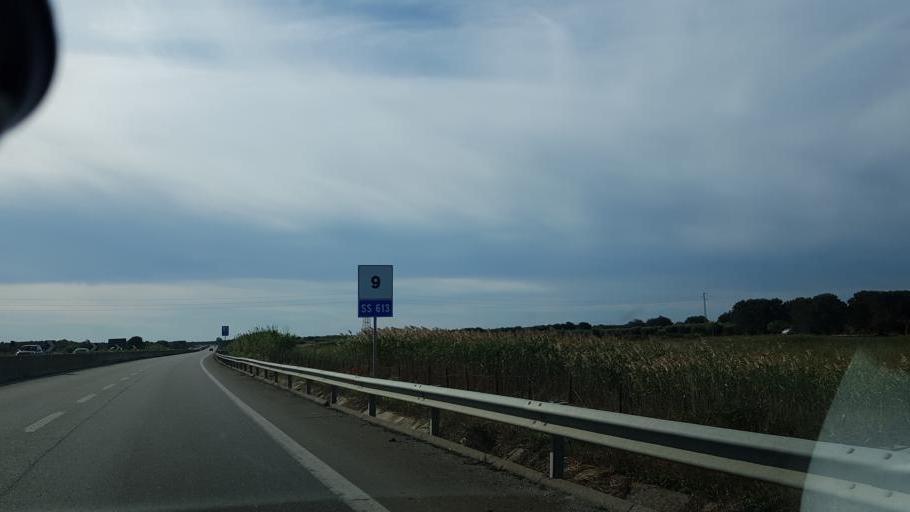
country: IT
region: Apulia
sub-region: Provincia di Brindisi
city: Tuturano
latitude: 40.5499
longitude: 17.9973
